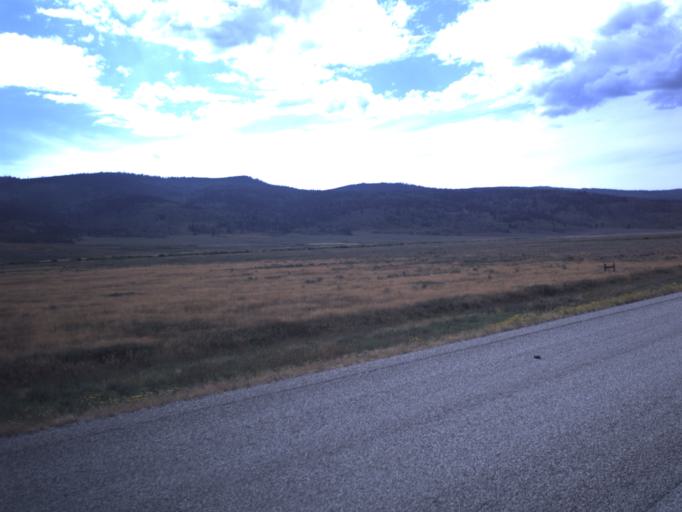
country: US
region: Utah
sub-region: Wasatch County
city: Heber
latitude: 40.2556
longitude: -111.2000
